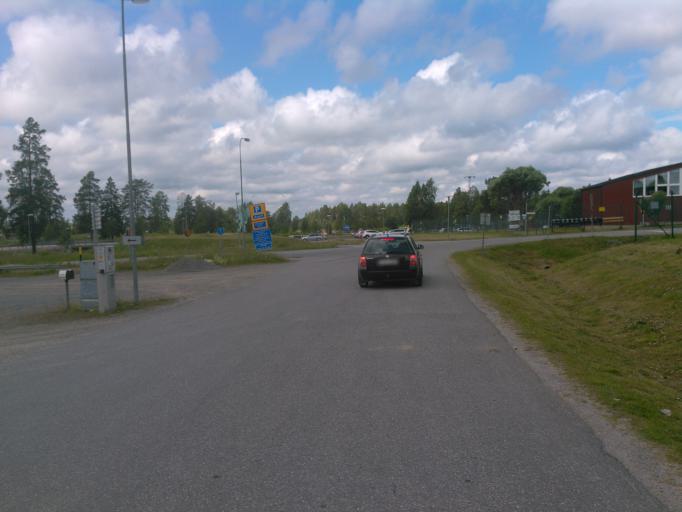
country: SE
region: Vaesterbotten
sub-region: Umea Kommun
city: Umea
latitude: 63.8365
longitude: 20.2542
